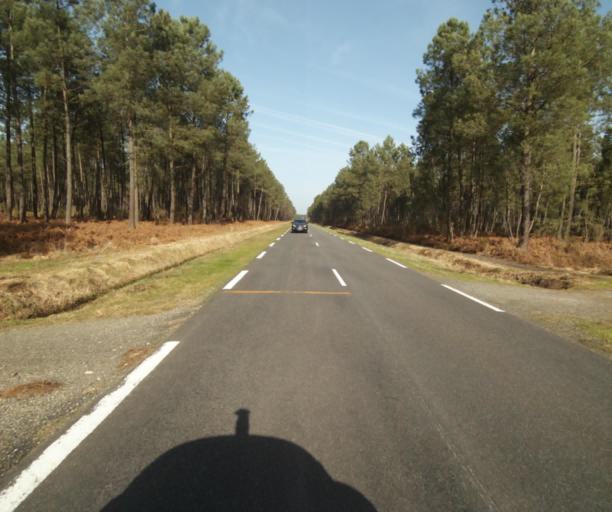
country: FR
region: Aquitaine
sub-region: Departement du Lot-et-Garonne
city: Casteljaloux
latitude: 44.1662
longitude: 0.0418
